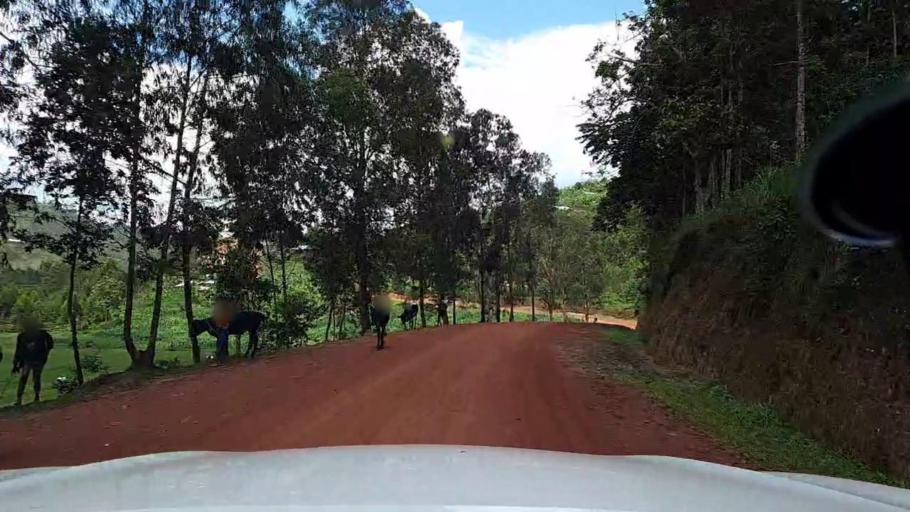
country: RW
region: Northern Province
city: Byumba
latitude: -1.7055
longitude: 29.8398
